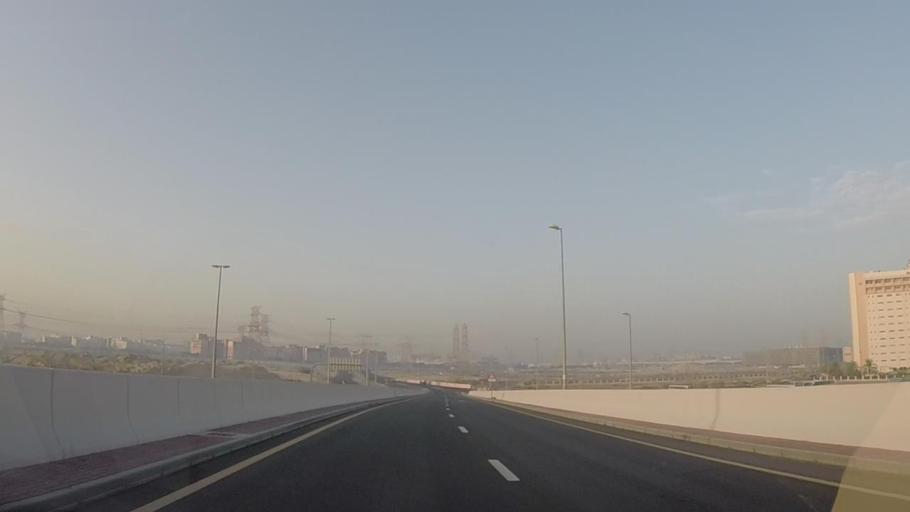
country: AE
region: Dubai
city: Dubai
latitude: 25.0535
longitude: 55.1338
